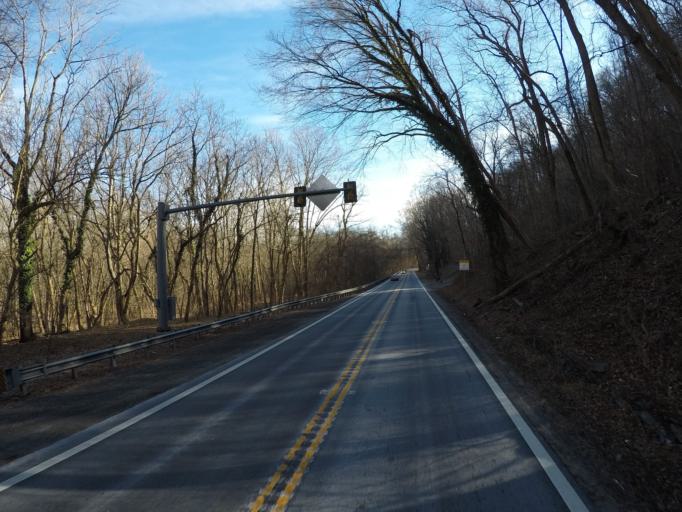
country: US
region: Maryland
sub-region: Frederick County
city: Point of Rocks
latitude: 39.2697
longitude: -77.5473
